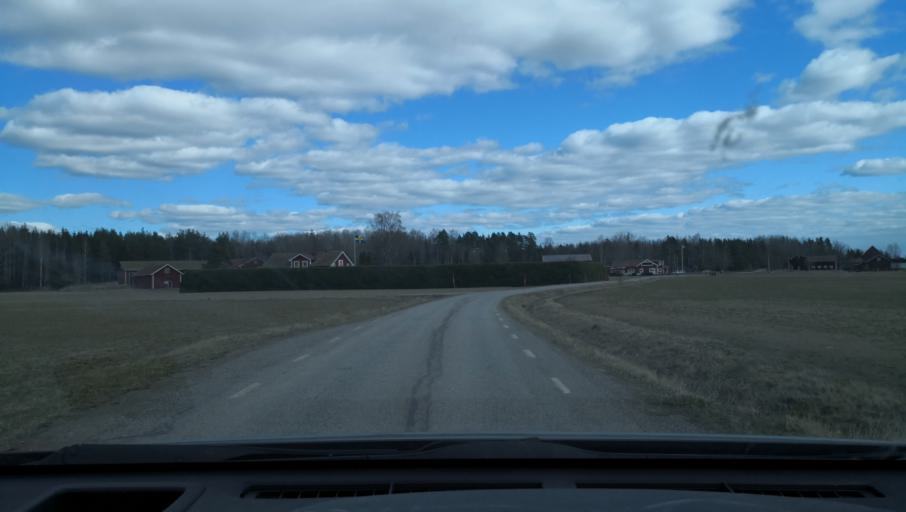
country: SE
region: Vaestmanland
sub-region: Sala Kommun
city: Sala
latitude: 59.8620
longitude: 16.5923
